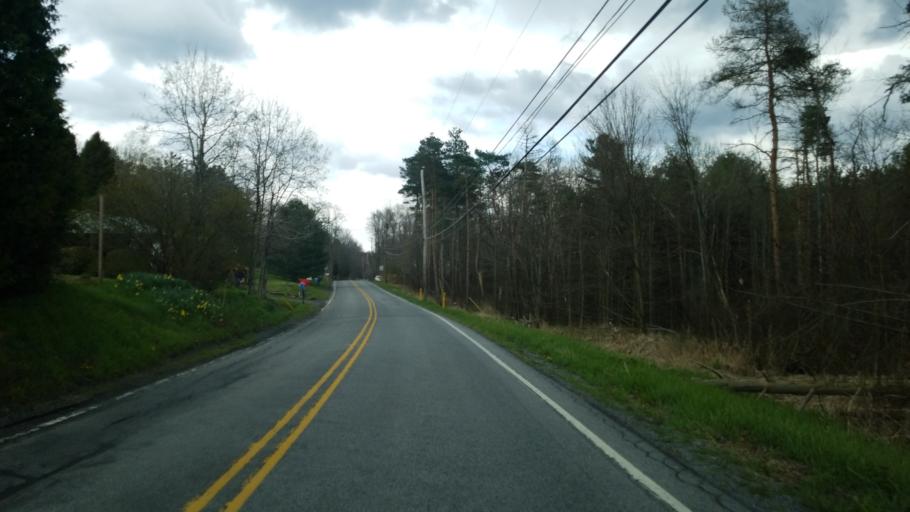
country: US
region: Pennsylvania
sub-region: Clearfield County
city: Curwensville
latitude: 40.8944
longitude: -78.4739
